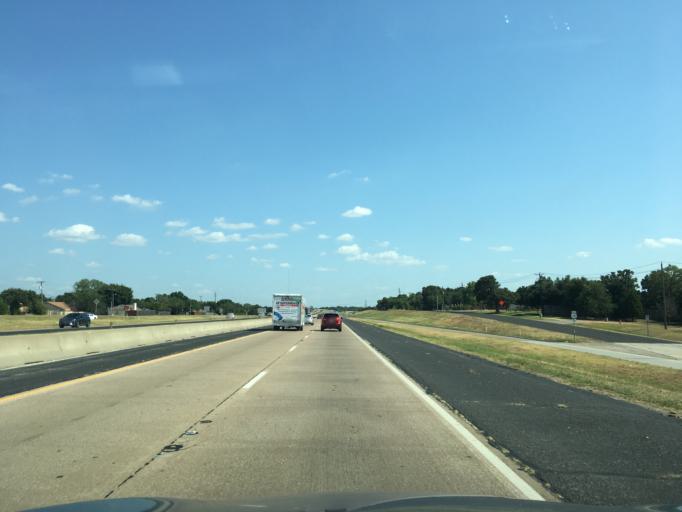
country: US
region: Texas
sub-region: Tarrant County
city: Kennedale
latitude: 32.6449
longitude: -97.1845
